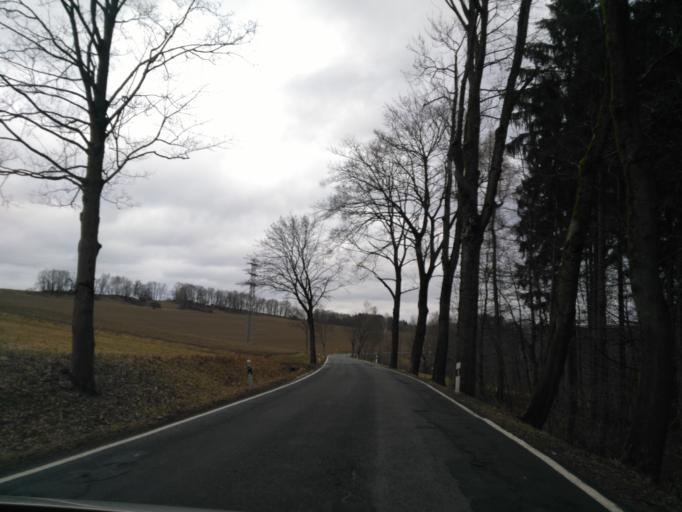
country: DE
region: Saxony
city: Venusberg
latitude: 50.6989
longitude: 12.9911
